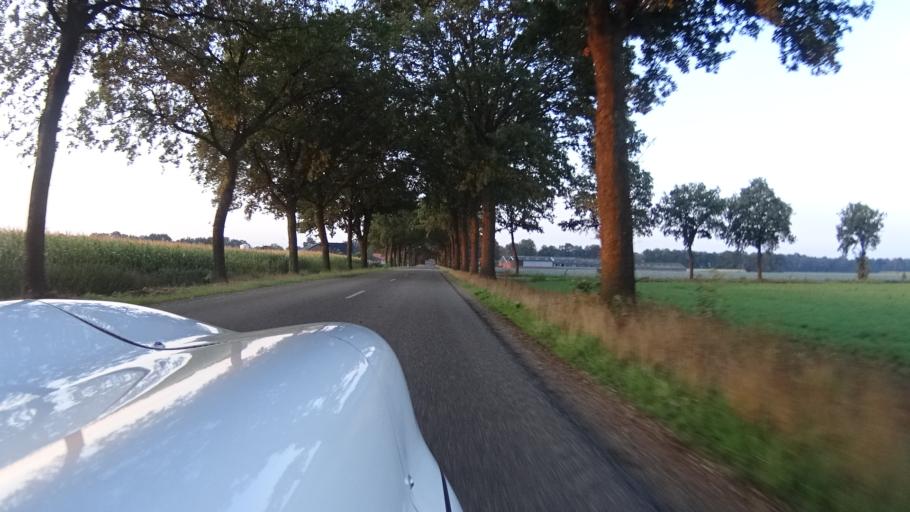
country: NL
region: North Brabant
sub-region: Gemeente Mill en Sint Hubert
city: Wilbertoord
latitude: 51.6086
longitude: 5.7830
